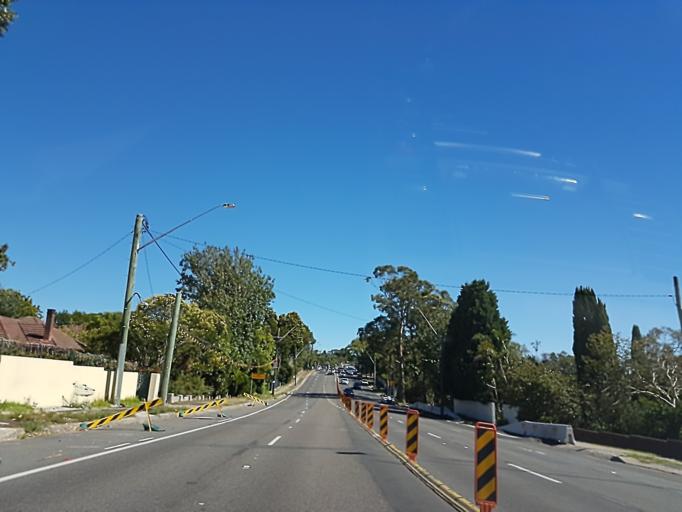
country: AU
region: New South Wales
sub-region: Warringah
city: Davidson
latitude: -33.7481
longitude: 151.2238
